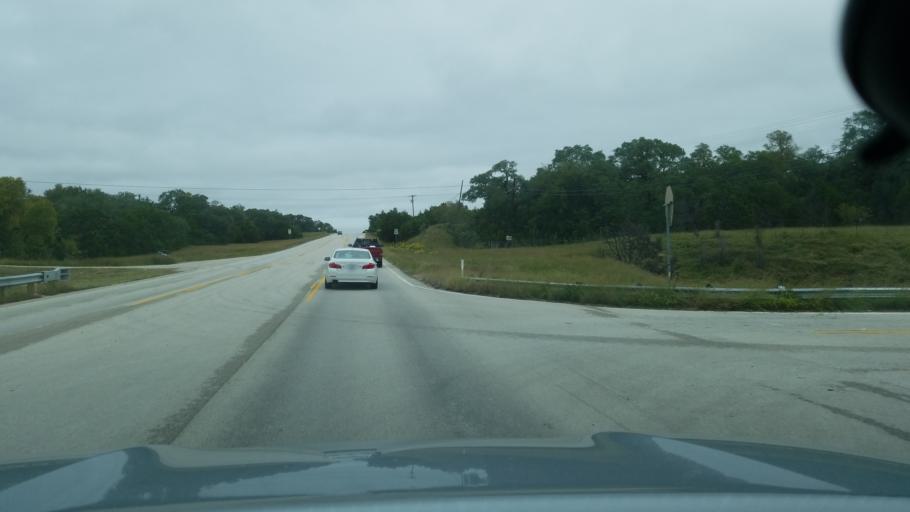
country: US
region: Texas
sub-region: Blanco County
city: Blanco
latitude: 30.0022
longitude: -98.4055
